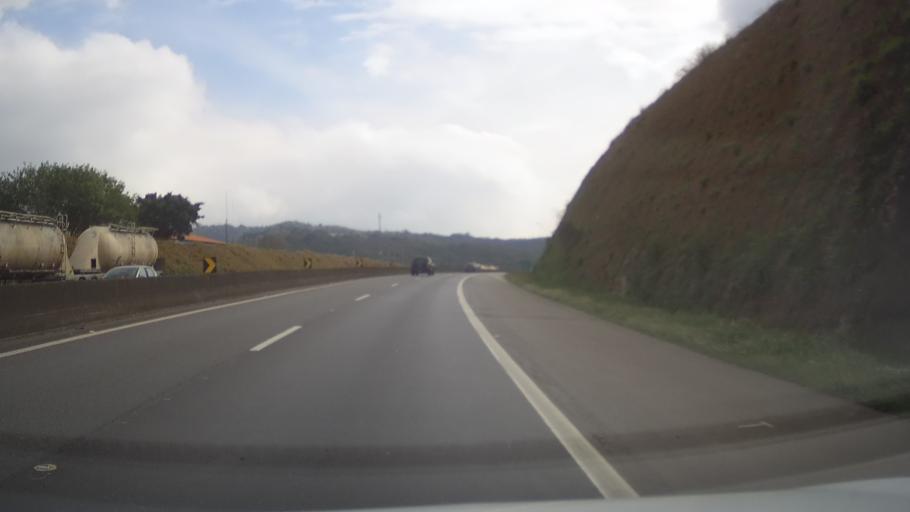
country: BR
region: Minas Gerais
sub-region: Extrema
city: Extrema
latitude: -22.8852
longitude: -46.4103
